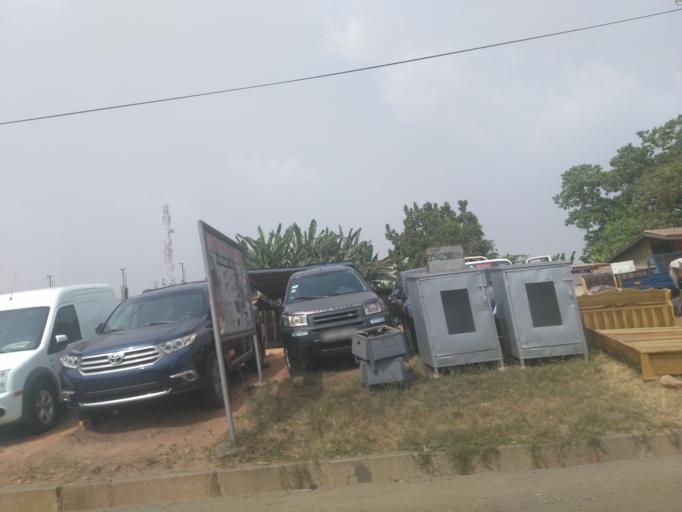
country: GH
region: Ashanti
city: Kumasi
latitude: 6.6875
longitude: -1.5806
